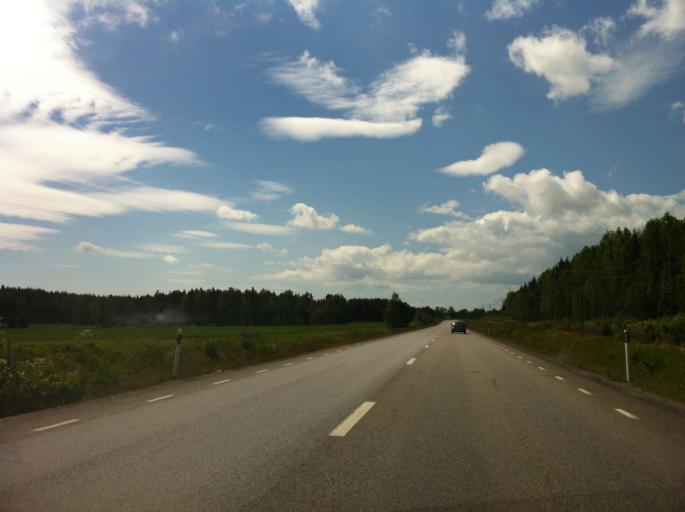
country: SE
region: Vaermland
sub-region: Saffle Kommun
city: Saeffle
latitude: 59.1707
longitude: 13.0026
